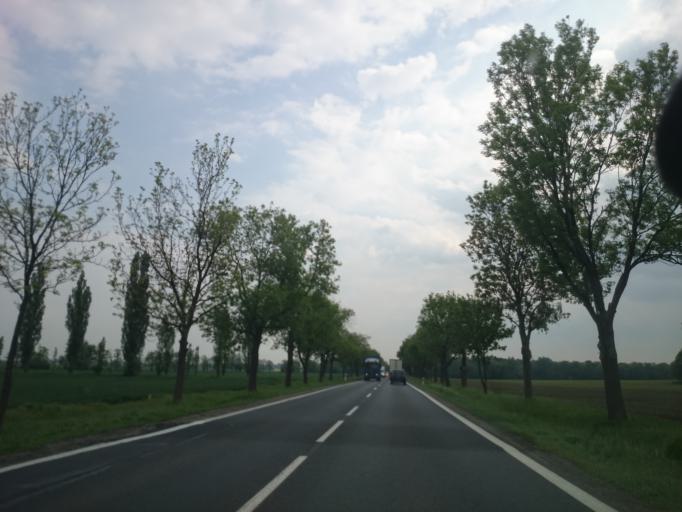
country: PL
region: Lower Silesian Voivodeship
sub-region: Powiat wroclawski
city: Kobierzyce
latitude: 50.9872
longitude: 16.9493
